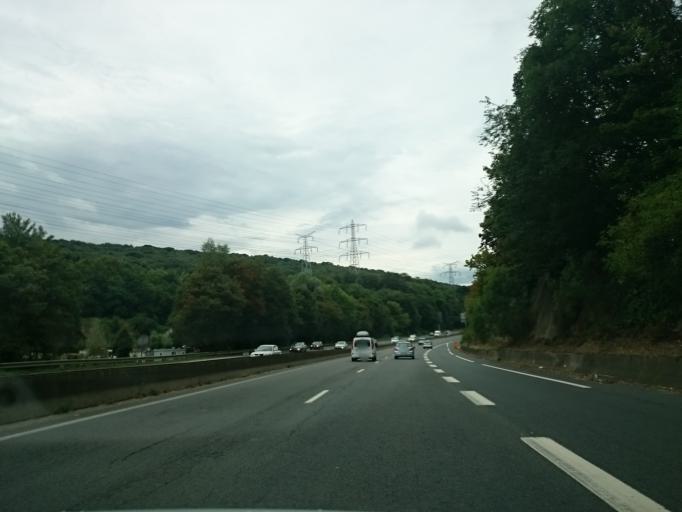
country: FR
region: Ile-de-France
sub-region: Departement de l'Essonne
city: Bievres
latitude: 48.7651
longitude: 2.2296
